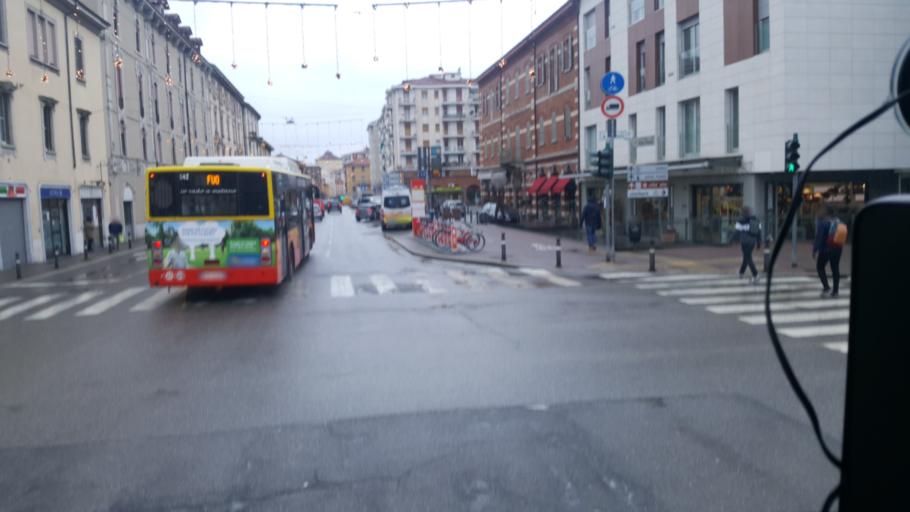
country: IT
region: Lombardy
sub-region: Provincia di Bergamo
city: Orio al Serio
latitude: 45.6946
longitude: 9.6887
